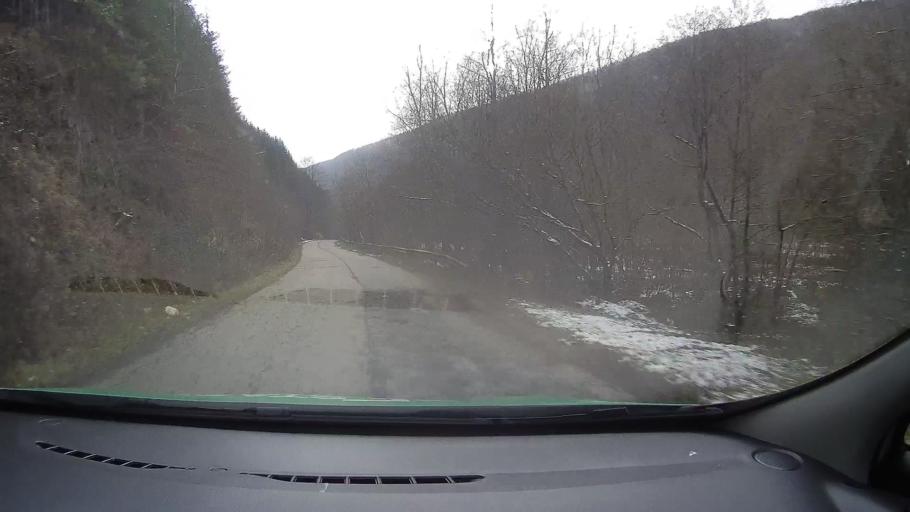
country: RO
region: Hunedoara
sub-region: Comuna Balsa
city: Balsa
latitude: 46.0034
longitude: 23.1502
